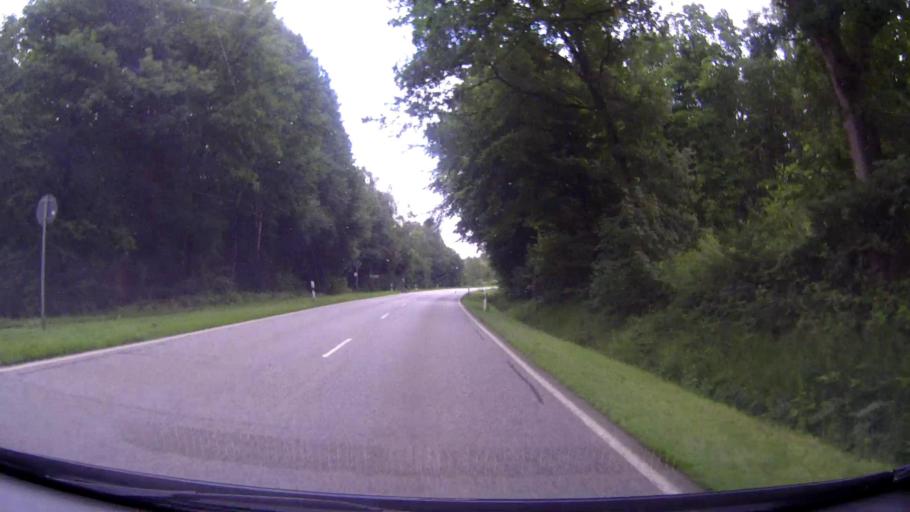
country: DE
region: Schleswig-Holstein
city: Meezen
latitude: 54.0738
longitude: 9.7276
